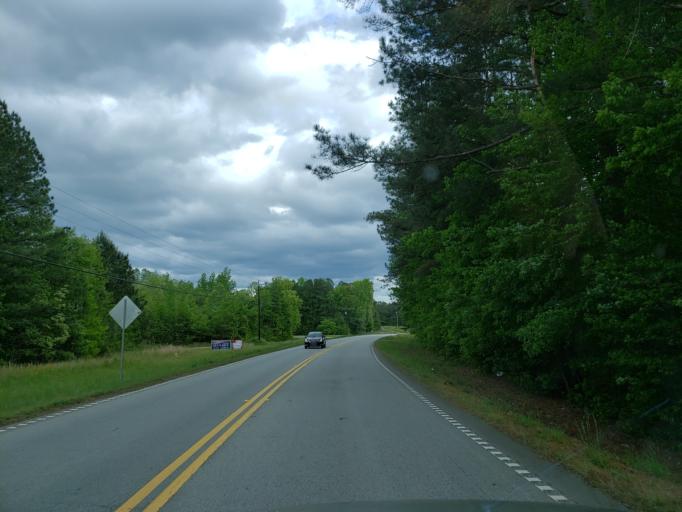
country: US
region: Georgia
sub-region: Haralson County
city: Tallapoosa
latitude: 33.8652
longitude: -85.2977
